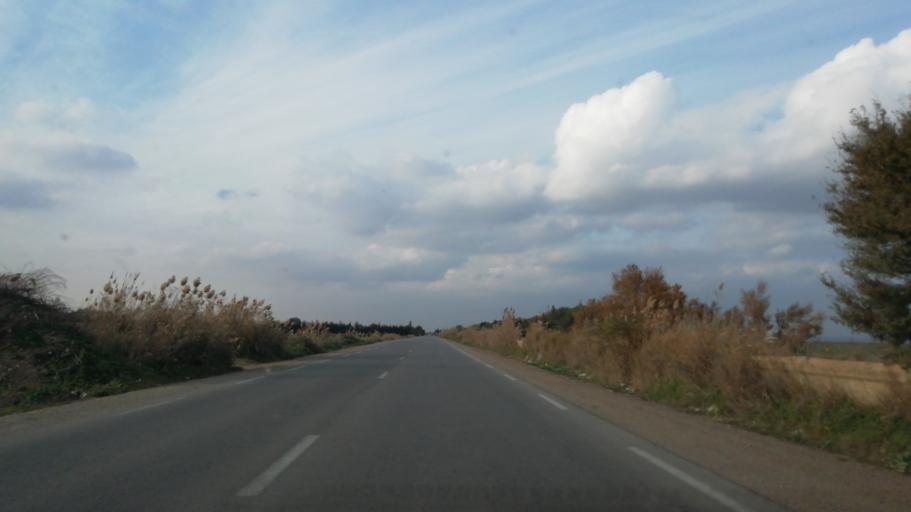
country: DZ
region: Mascara
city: Sig
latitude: 35.6399
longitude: 0.0325
